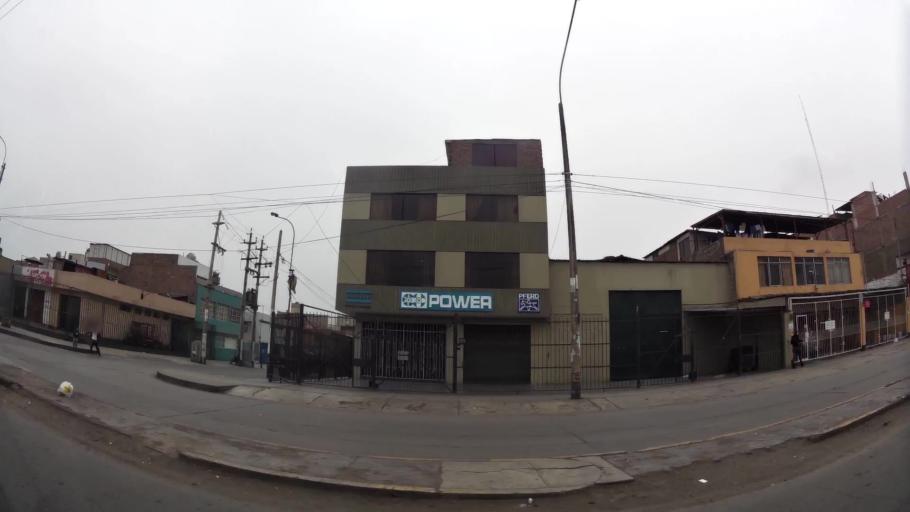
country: PE
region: Lima
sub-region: Lima
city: San Luis
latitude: -12.0815
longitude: -77.0133
